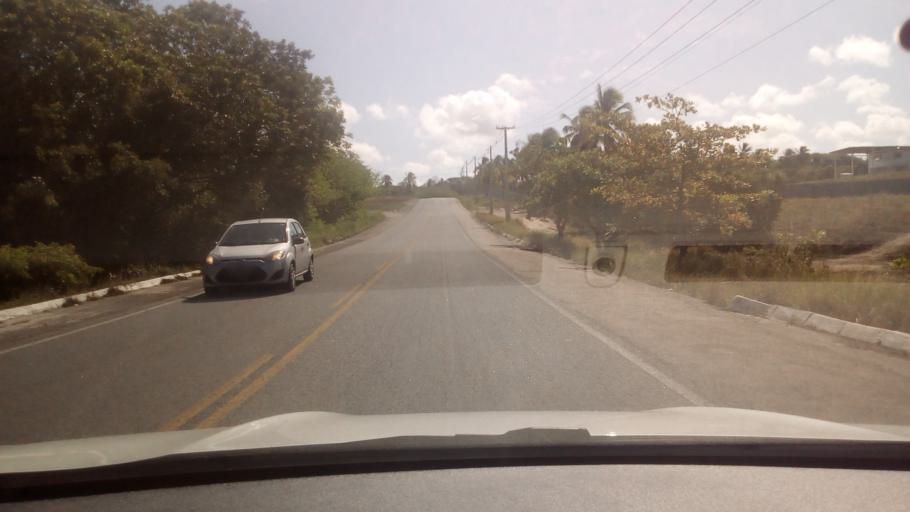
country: BR
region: Paraiba
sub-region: Joao Pessoa
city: Joao Pessoa
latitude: -7.1971
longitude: -34.8077
